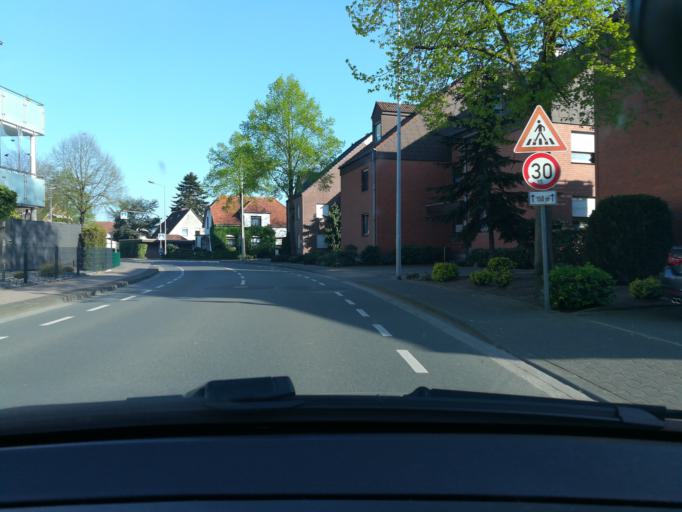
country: DE
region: North Rhine-Westphalia
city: Versmold
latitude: 52.0376
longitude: 8.1544
